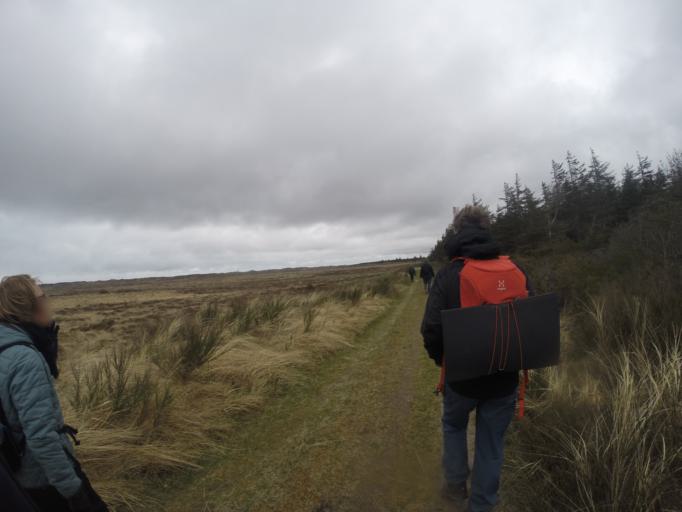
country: DK
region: North Denmark
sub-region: Thisted Kommune
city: Hurup
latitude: 56.9045
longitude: 8.3434
